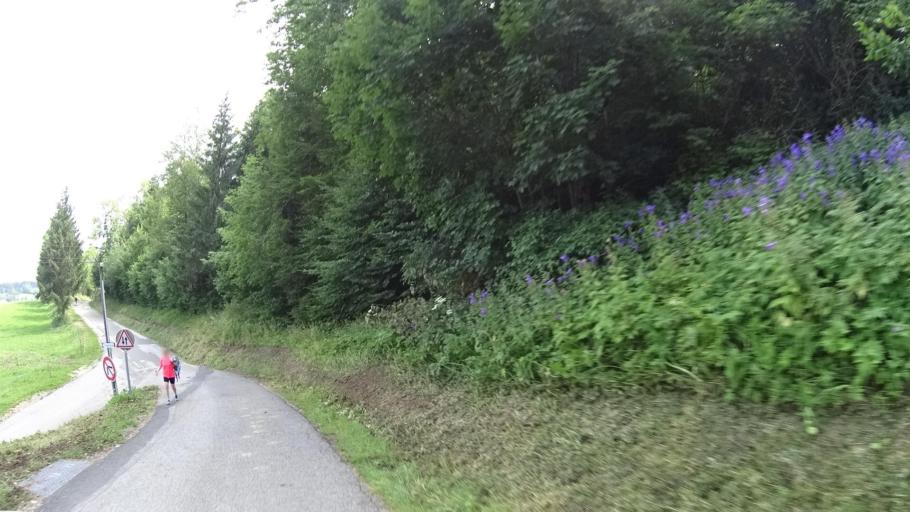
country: FR
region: Franche-Comte
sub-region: Departement du Doubs
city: Les Fourgs
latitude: 46.8276
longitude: 6.3347
